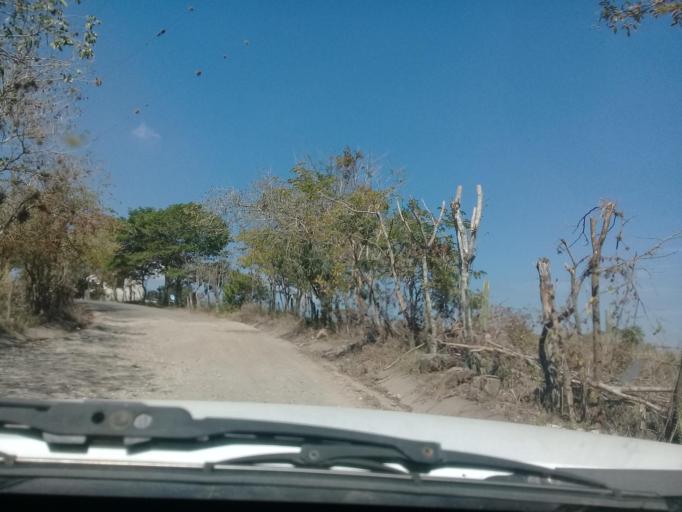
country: MX
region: Veracruz
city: Actopan
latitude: 19.4770
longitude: -96.6421
